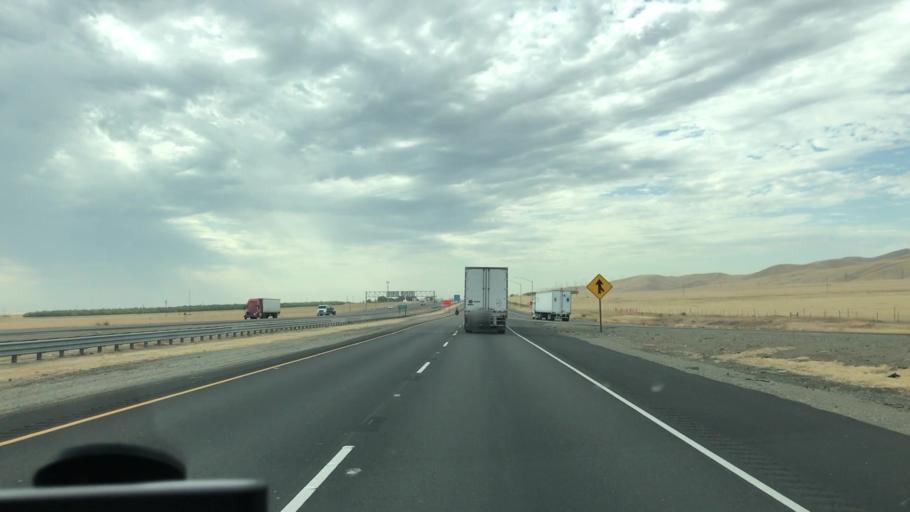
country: US
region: California
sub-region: San Joaquin County
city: Tracy
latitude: 37.5921
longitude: -121.3355
